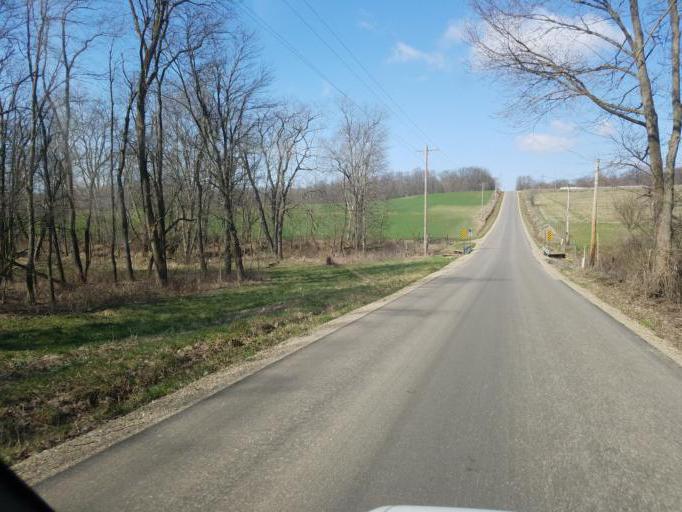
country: US
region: Ohio
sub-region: Licking County
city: Utica
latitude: 40.2476
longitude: -82.3442
